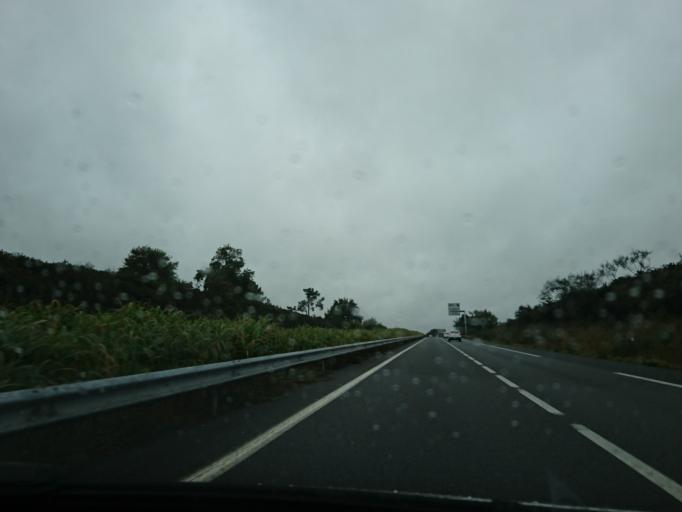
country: FR
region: Brittany
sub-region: Departement du Morbihan
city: Nivillac
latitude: 47.5065
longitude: -2.2701
